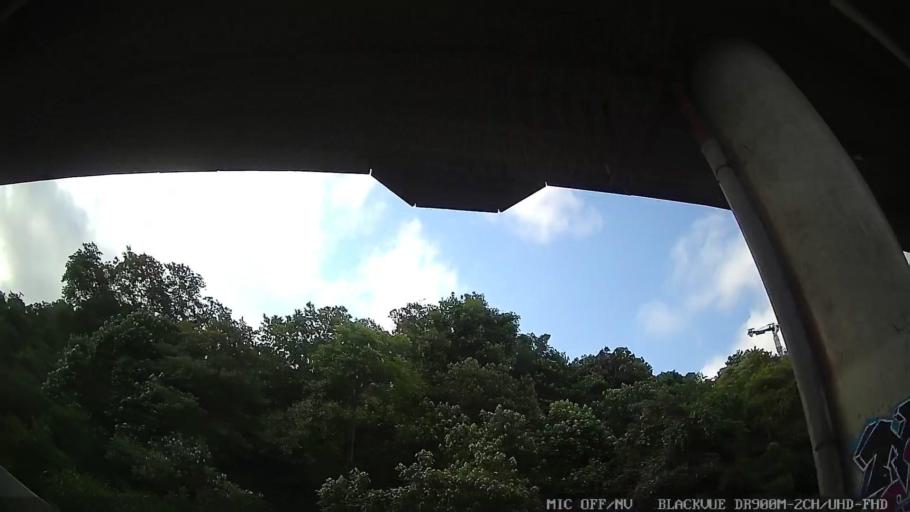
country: BR
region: Sao Paulo
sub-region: Taboao Da Serra
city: Taboao da Serra
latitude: -23.6447
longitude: -46.7496
